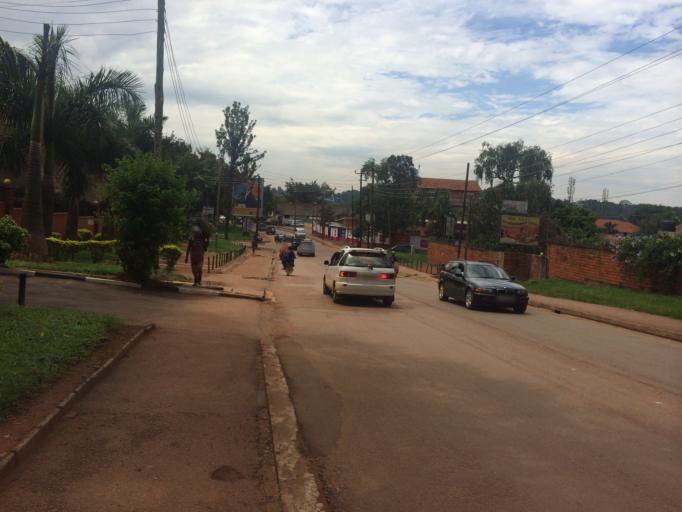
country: UG
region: Central Region
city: Kampala Central Division
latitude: 0.3342
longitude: 32.5877
